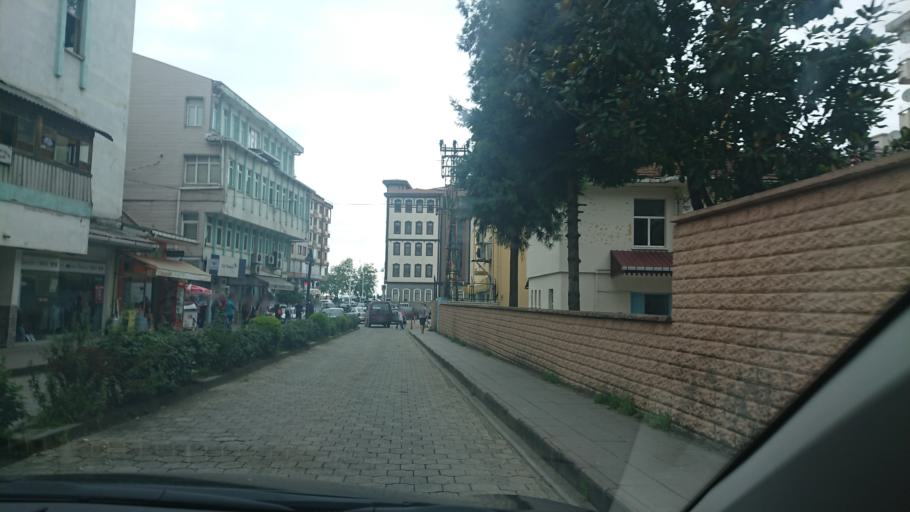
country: TR
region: Rize
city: Cayeli
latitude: 41.0888
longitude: 40.7259
